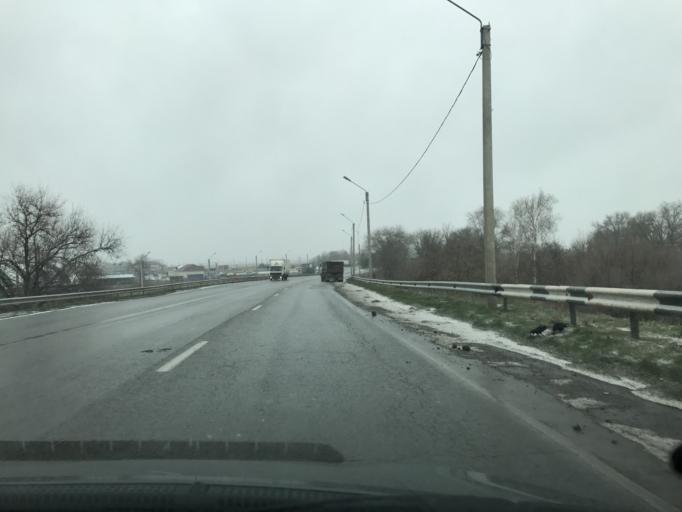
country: RU
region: Rostov
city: Bataysk
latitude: 47.0830
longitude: 39.7695
